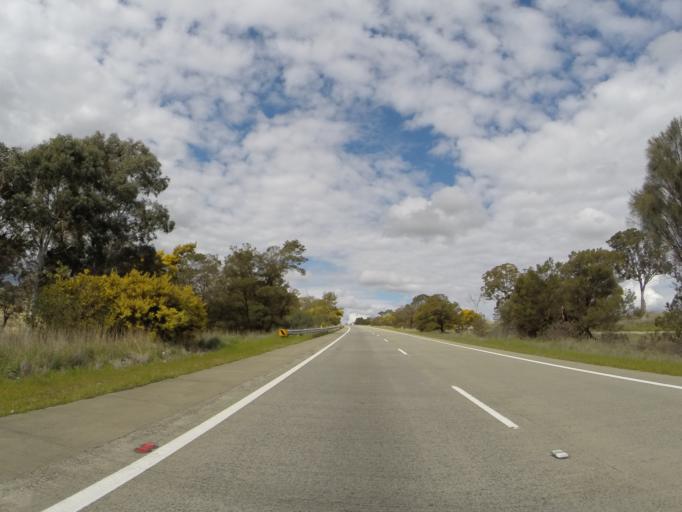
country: AU
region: New South Wales
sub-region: Yass Valley
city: Gundaroo
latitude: -34.8192
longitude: 149.3445
